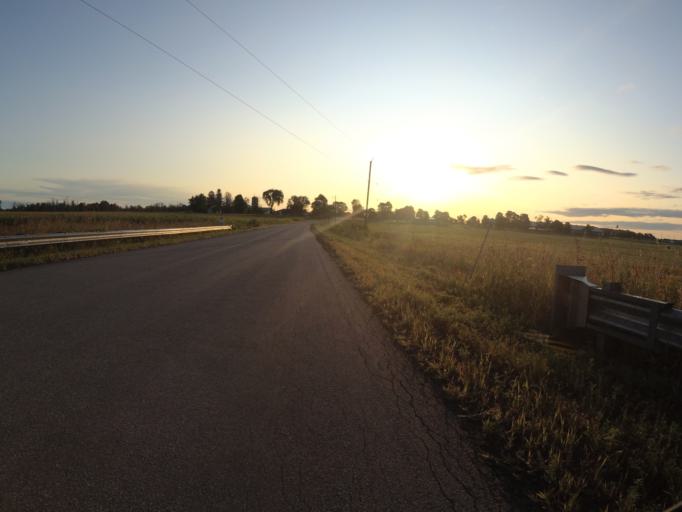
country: CA
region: Ontario
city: Ottawa
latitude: 45.1212
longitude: -75.5086
